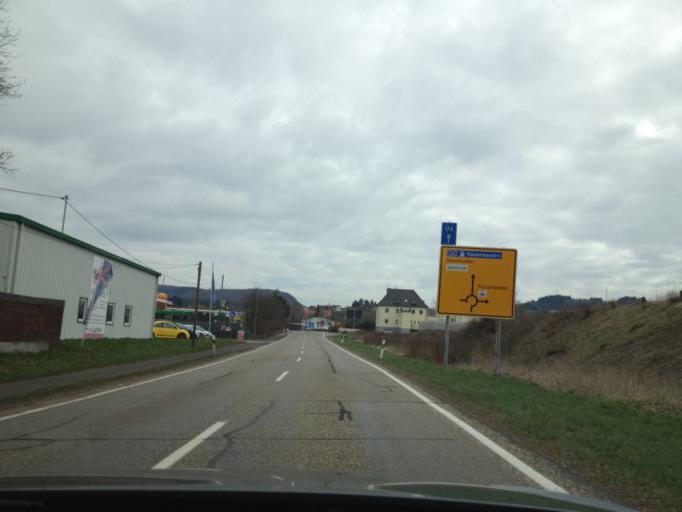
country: DE
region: Saarland
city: Freisen
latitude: 49.5522
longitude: 7.2371
